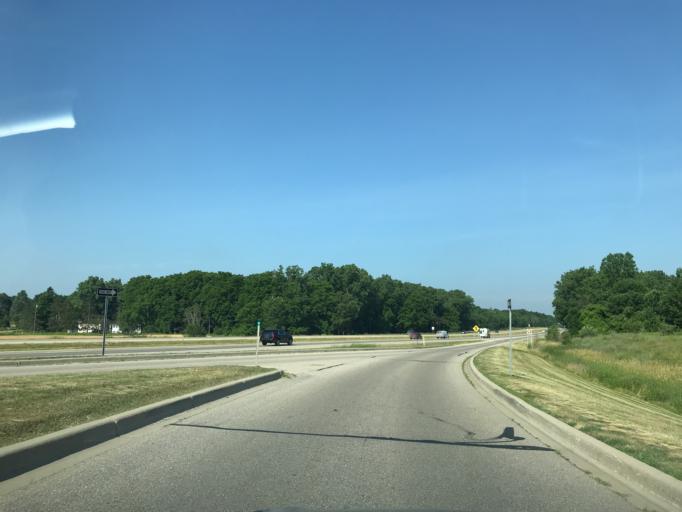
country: US
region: Michigan
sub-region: Ingham County
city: Okemos
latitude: 42.6773
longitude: -84.4083
